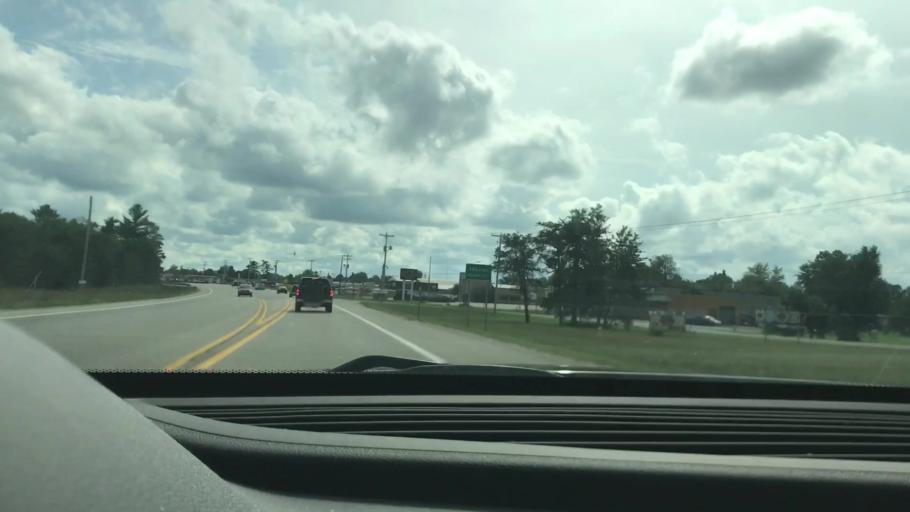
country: US
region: Michigan
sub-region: Kalkaska County
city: Kalkaska
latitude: 44.7485
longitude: -85.1735
